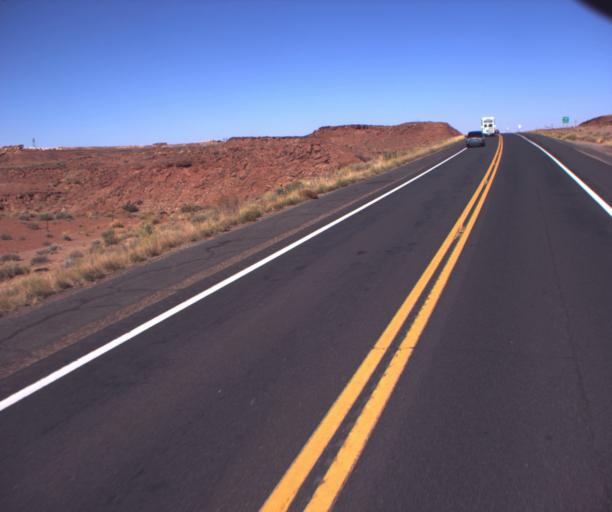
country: US
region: Arizona
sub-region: Coconino County
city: Tuba City
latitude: 35.7905
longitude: -111.4499
